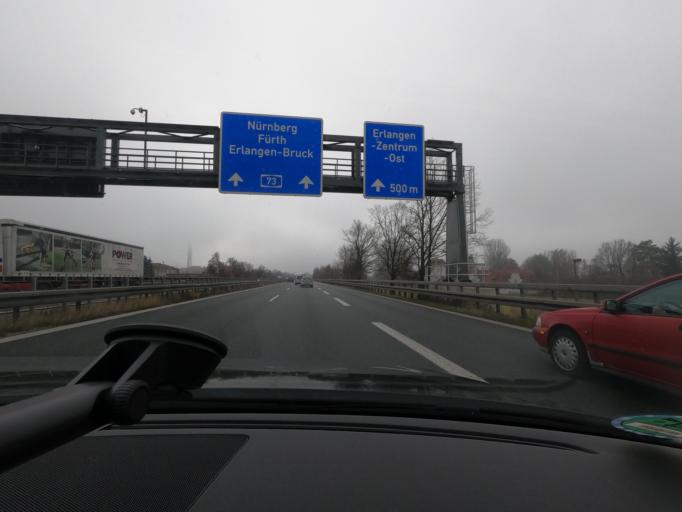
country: DE
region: Bavaria
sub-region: Regierungsbezirk Mittelfranken
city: Erlangen
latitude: 49.6003
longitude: 10.9982
